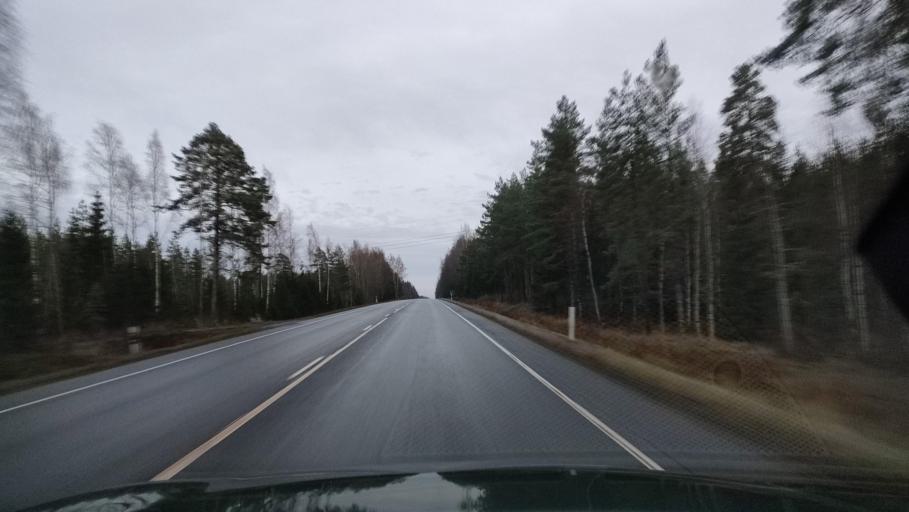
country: FI
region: Ostrobothnia
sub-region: Vaasa
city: Ristinummi
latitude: 63.0183
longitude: 21.7587
